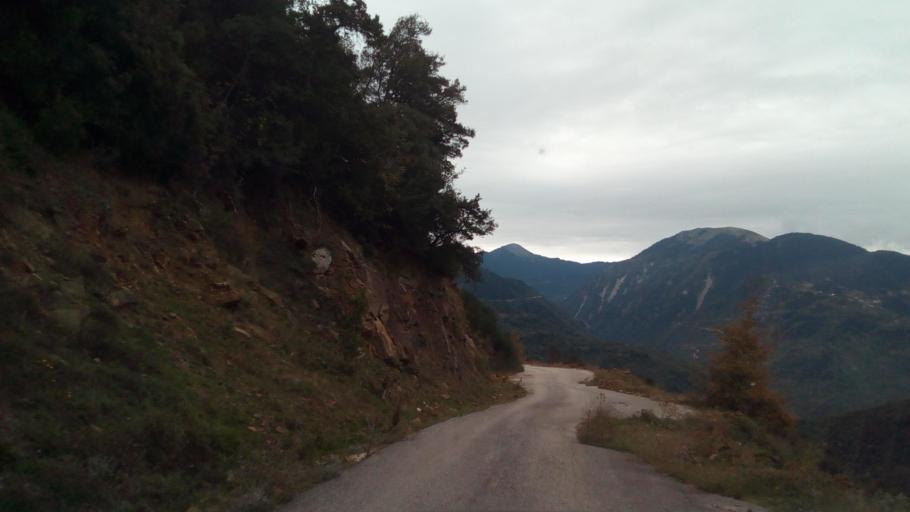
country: GR
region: West Greece
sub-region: Nomos Aitolias kai Akarnanias
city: Thermo
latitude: 38.6071
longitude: 21.8444
